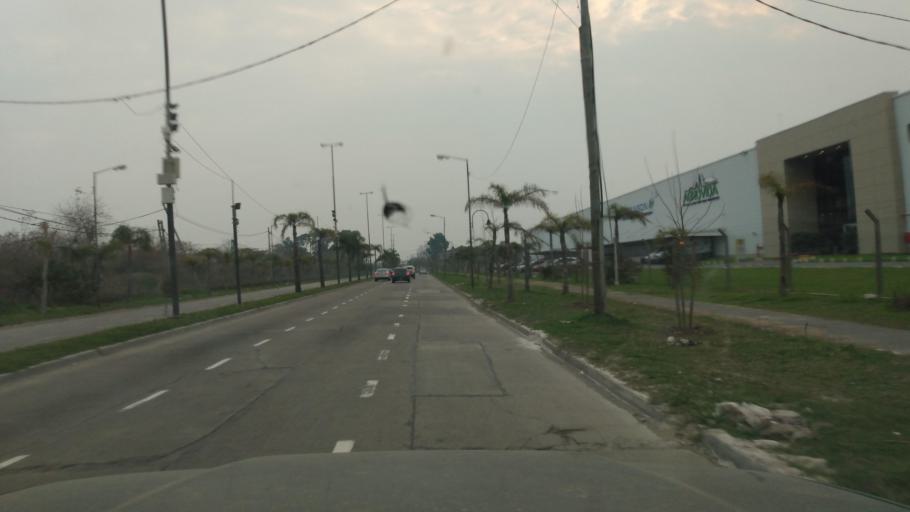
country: AR
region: Buenos Aires
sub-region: Partido de Tigre
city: Tigre
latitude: -34.4591
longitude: -58.5899
